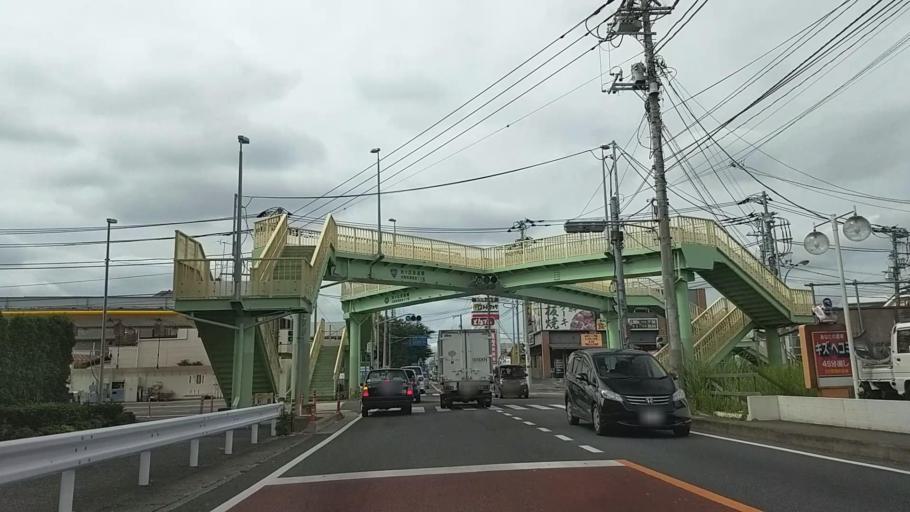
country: JP
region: Kanagawa
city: Minami-rinkan
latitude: 35.4629
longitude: 139.4672
